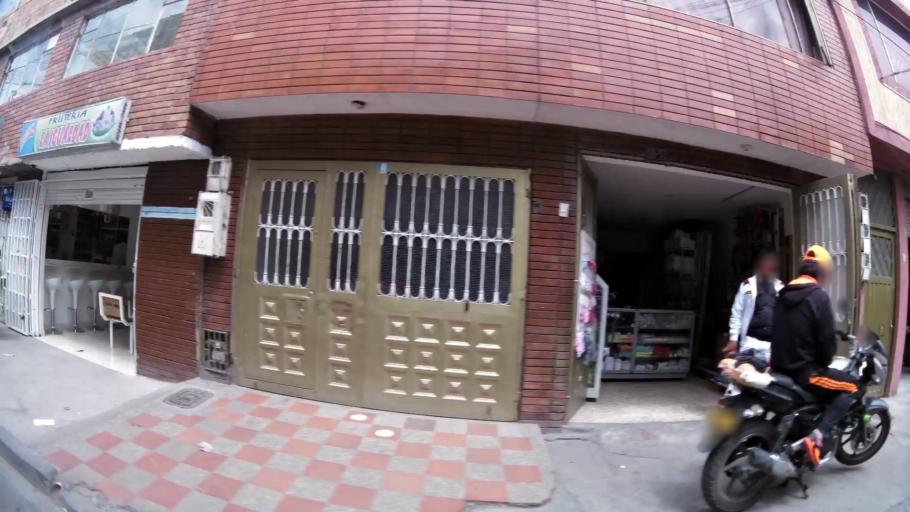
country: CO
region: Bogota D.C.
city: Bogota
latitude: 4.6216
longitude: -74.1280
